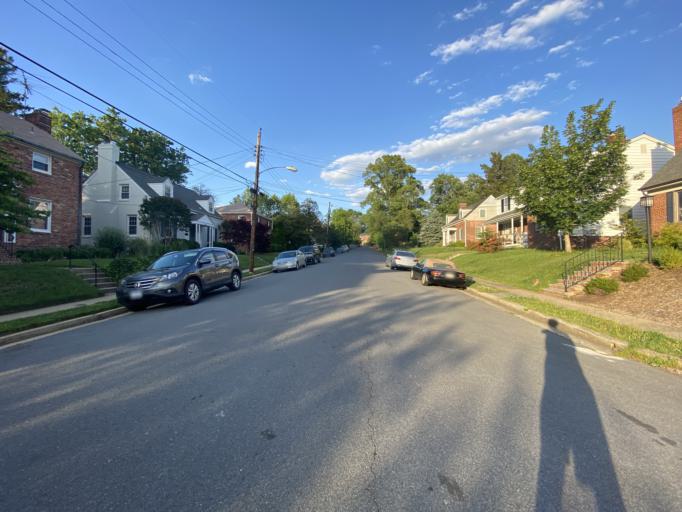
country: US
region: Virginia
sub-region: Fairfax County
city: Seven Corners
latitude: 38.8918
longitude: -77.1470
